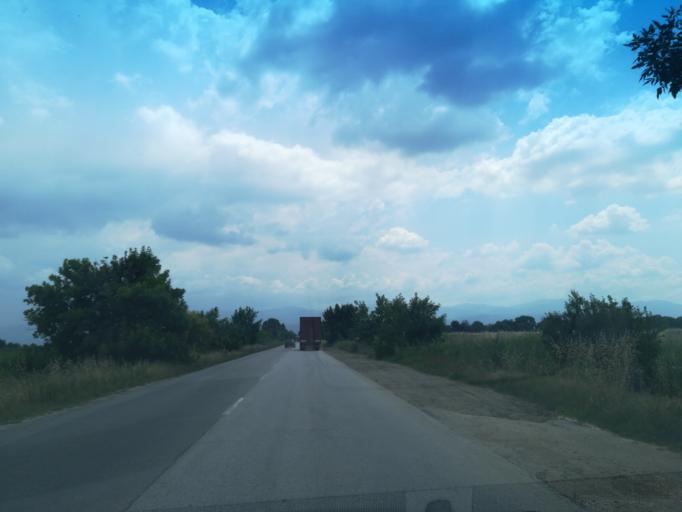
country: BG
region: Plovdiv
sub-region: Obshtina Plovdiv
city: Plovdiv
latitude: 42.1800
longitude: 24.6765
